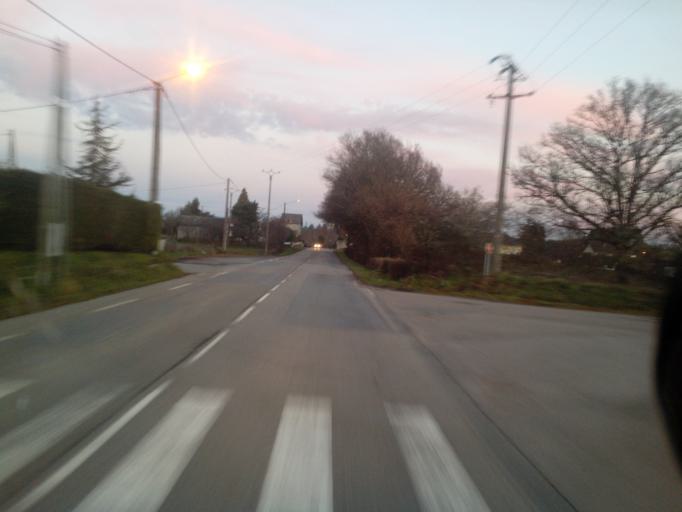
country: FR
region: Limousin
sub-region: Departement de la Correze
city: Meymac
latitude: 45.5032
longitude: 2.2241
